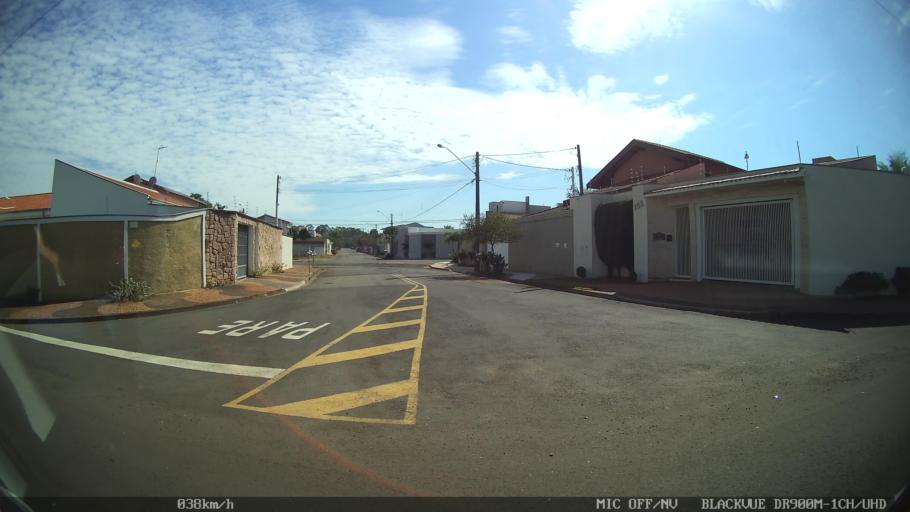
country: BR
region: Sao Paulo
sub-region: Santa Barbara D'Oeste
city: Santa Barbara d'Oeste
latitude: -22.7454
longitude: -47.4224
